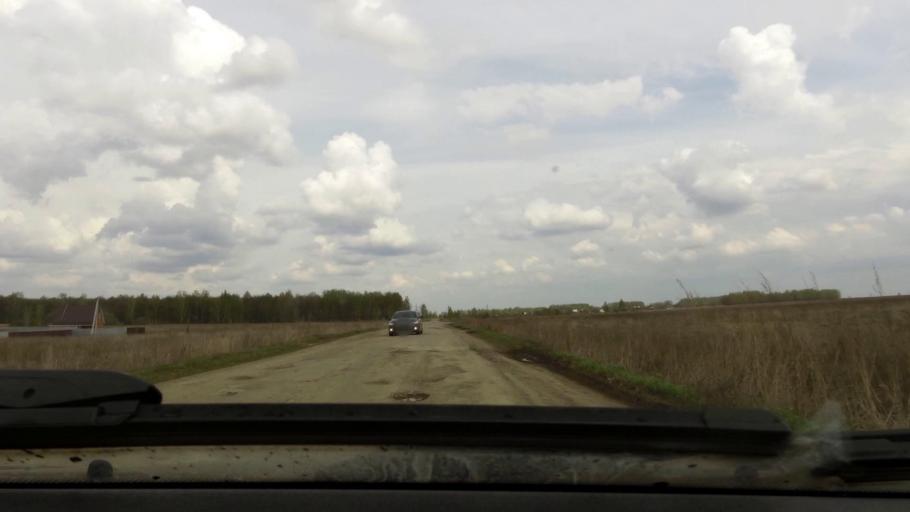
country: RU
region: Rjazan
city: Bagramovo
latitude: 54.7020
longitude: 39.3126
